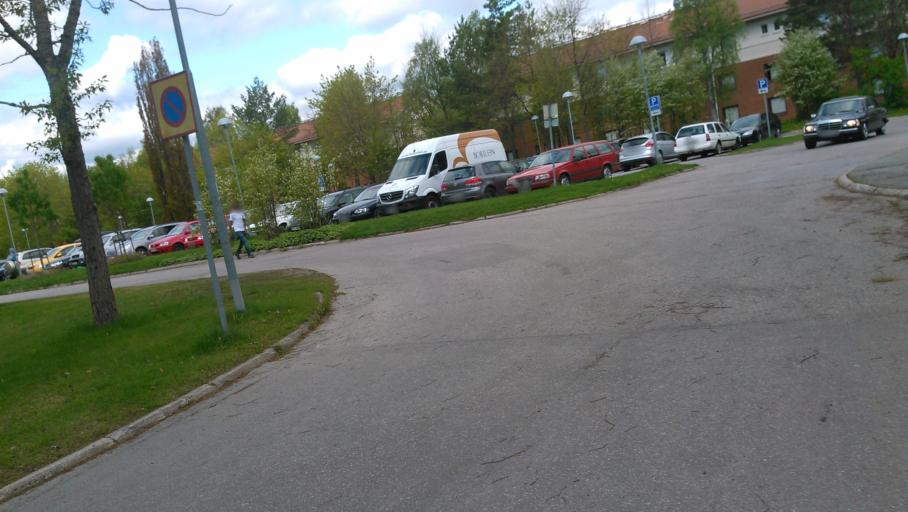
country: SE
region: Vaesterbotten
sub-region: Umea Kommun
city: Umea
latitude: 63.8109
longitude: 20.3115
